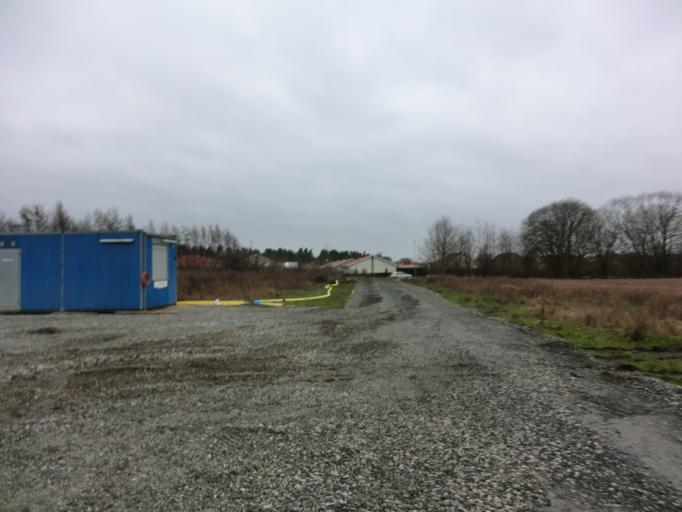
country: SE
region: Skane
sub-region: Eslovs Kommun
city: Eslov
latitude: 55.7244
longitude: 13.3561
